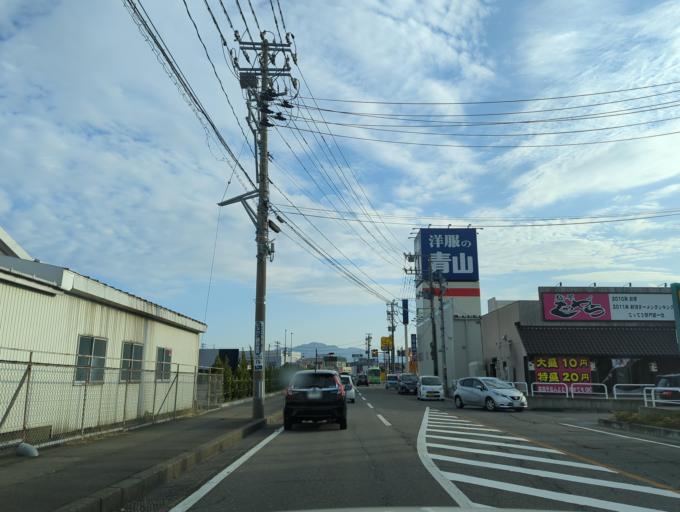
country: JP
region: Niigata
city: Kashiwazaki
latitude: 37.3620
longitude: 138.5636
